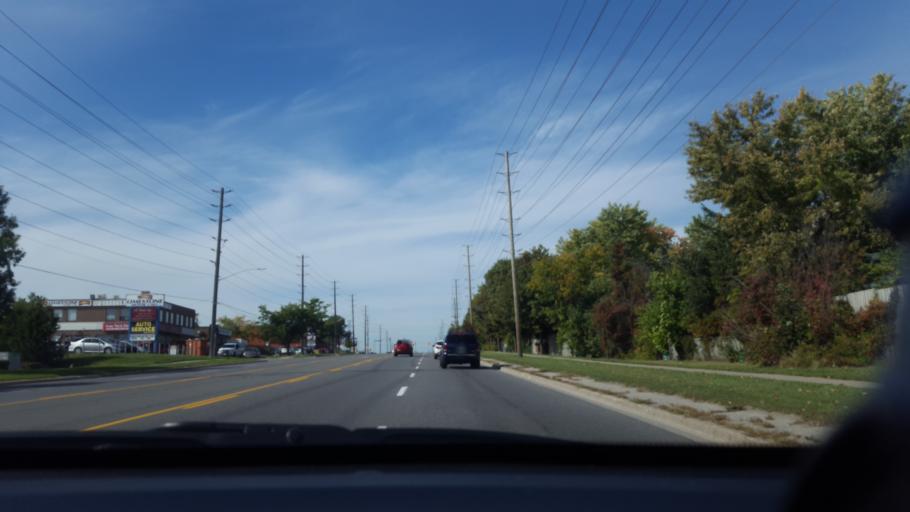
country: CA
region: Ontario
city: Newmarket
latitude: 44.0386
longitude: -79.4660
